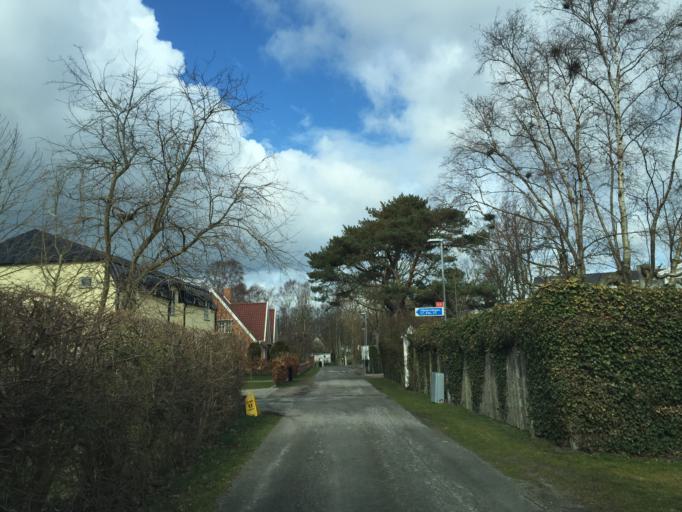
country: SE
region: Skane
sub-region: Vellinge Kommun
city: Skanor med Falsterbo
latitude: 55.3937
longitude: 12.8306
